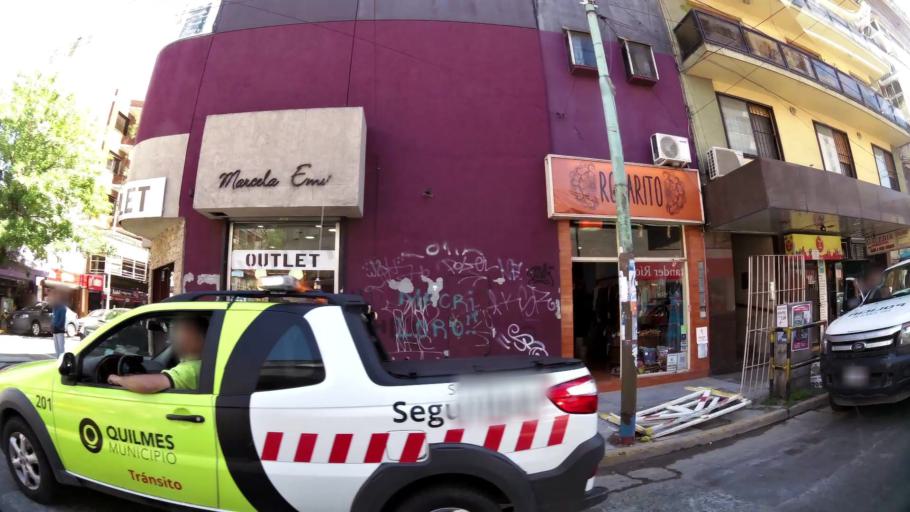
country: AR
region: Buenos Aires
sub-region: Partido de Quilmes
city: Quilmes
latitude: -34.7233
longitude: -58.2574
